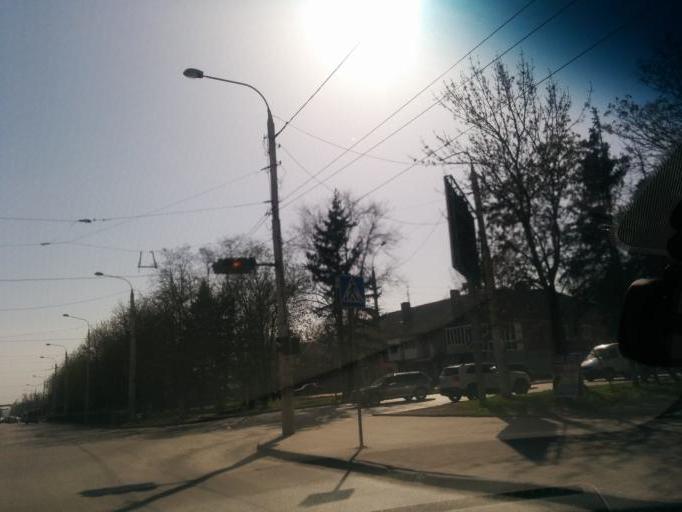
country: RU
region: Rostov
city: Shakhty
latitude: 47.7007
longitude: 40.2098
